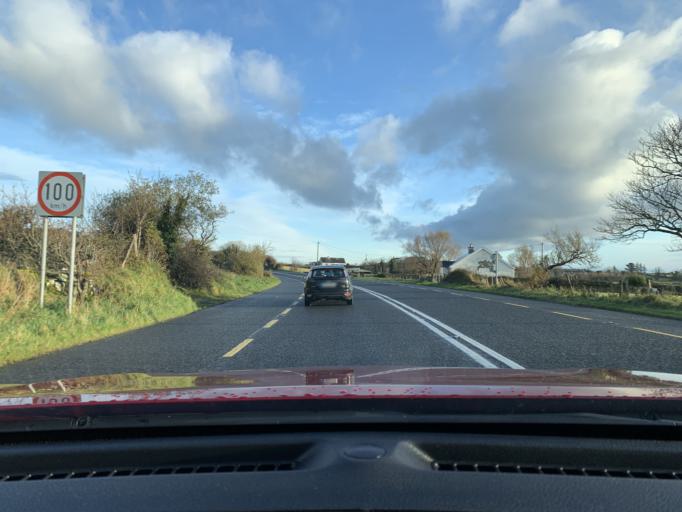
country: IE
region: Connaught
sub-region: Sligo
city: Sligo
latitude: 54.3978
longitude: -8.5123
